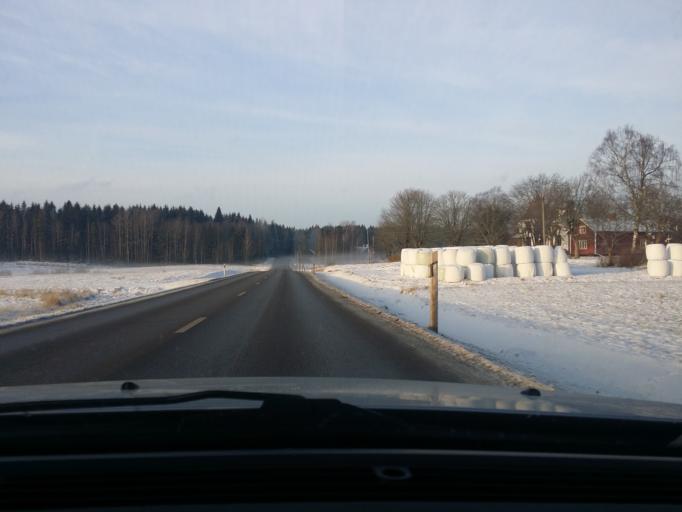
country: SE
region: OErebro
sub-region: Lindesbergs Kommun
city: Frovi
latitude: 59.5186
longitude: 15.3274
